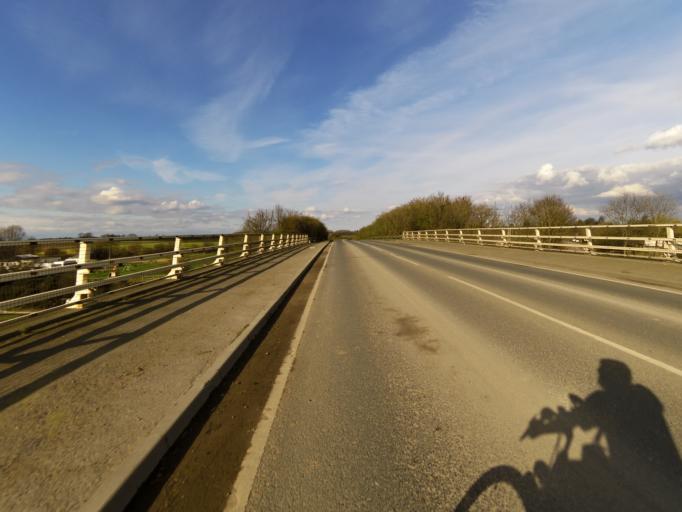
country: GB
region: England
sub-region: East Riding of Yorkshire
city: Pollington
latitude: 53.6808
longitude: -1.0560
